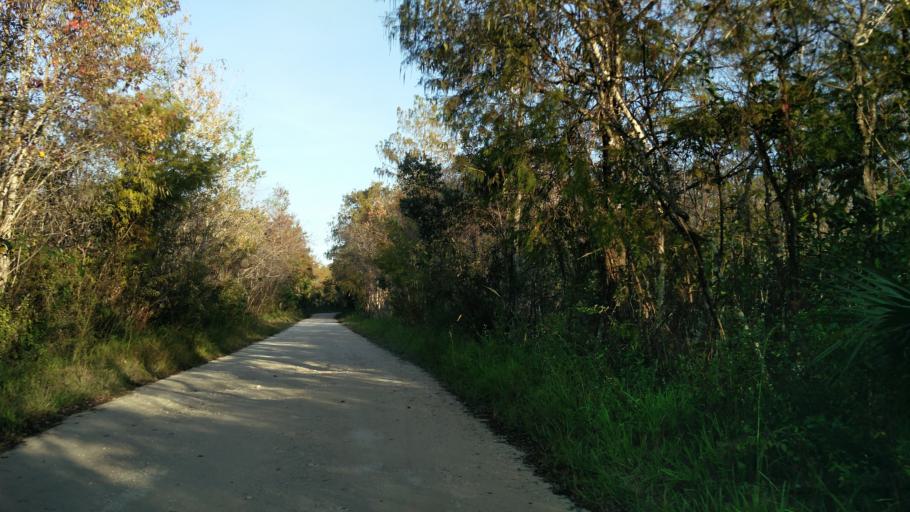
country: US
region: Florida
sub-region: Collier County
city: Lely Resort
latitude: 25.9801
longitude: -81.3754
